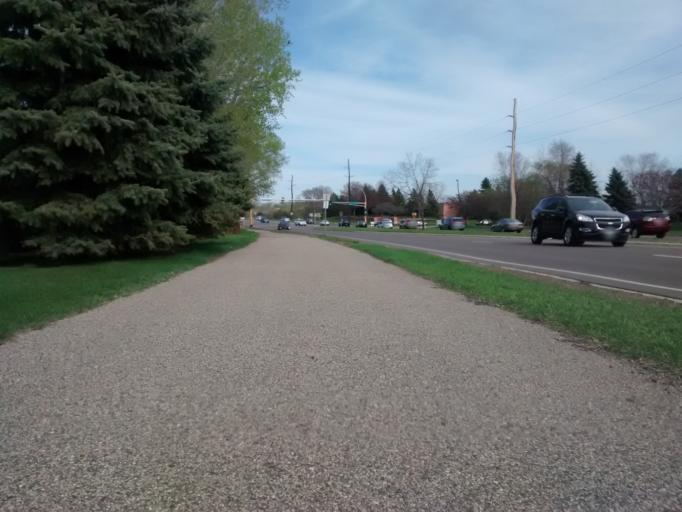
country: US
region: Minnesota
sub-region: Dakota County
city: Burnsville
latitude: 44.7523
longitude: -93.2899
